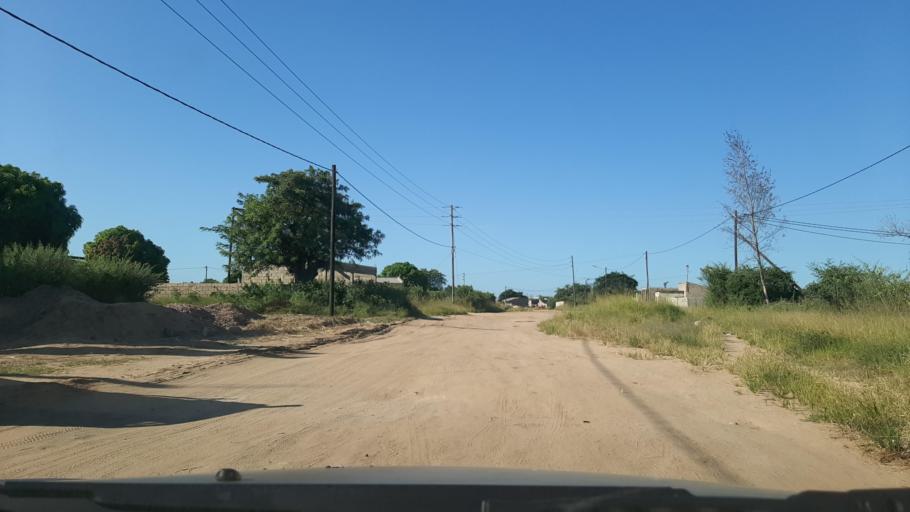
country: MZ
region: Maputo City
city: Maputo
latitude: -25.7597
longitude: 32.5495
